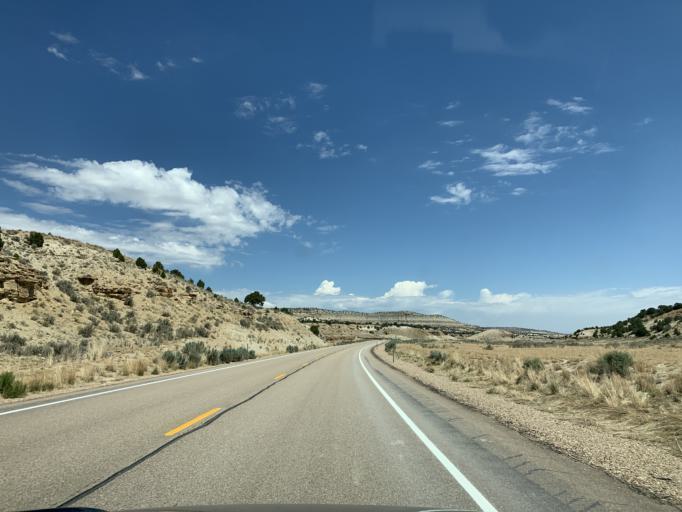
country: US
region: Utah
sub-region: Duchesne County
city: Duchesne
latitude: 39.9303
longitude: -110.2216
